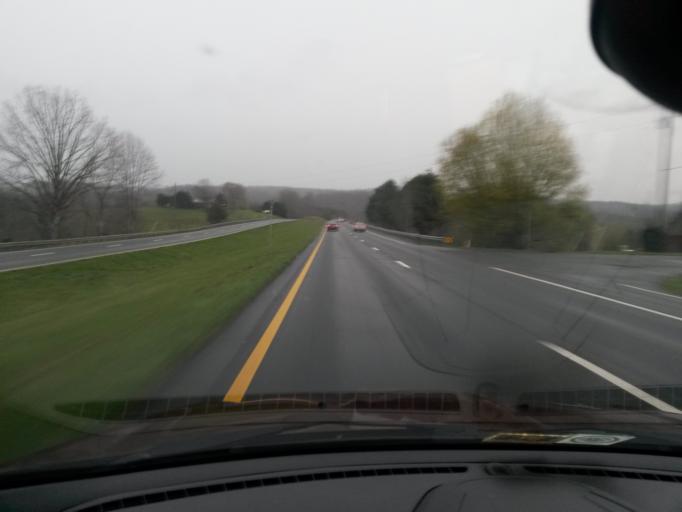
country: US
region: Virginia
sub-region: Bedford County
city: Forest
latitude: 37.3113
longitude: -79.4001
